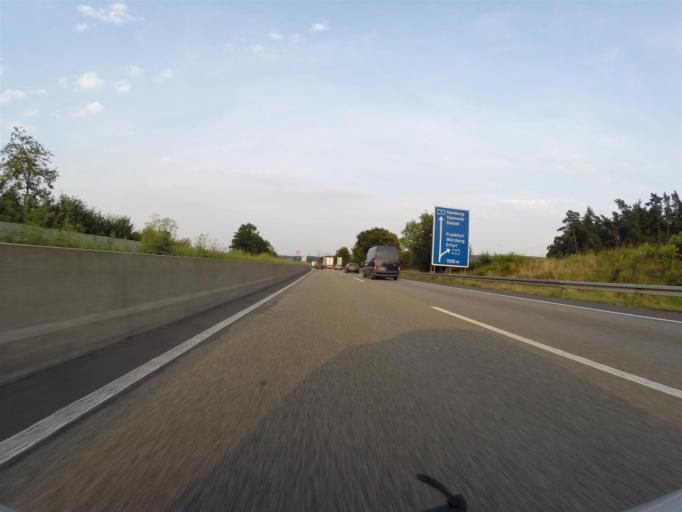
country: DE
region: Hesse
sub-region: Regierungsbezirk Kassel
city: Fuldabruck
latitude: 51.2594
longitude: 9.4893
